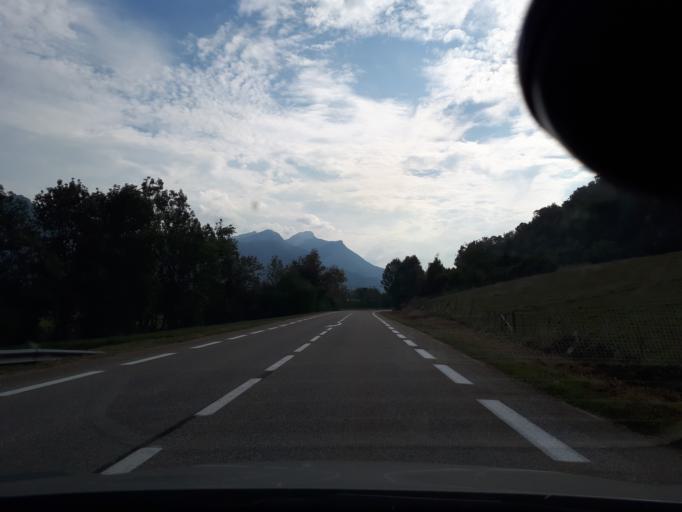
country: FR
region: Rhone-Alpes
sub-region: Departement de la Savoie
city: Les Echelles
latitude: 45.4445
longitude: 5.7625
